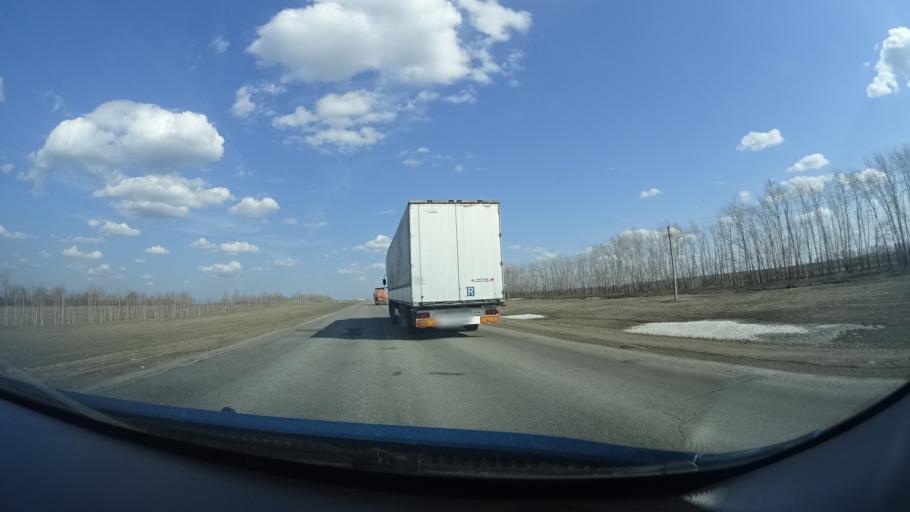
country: RU
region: Bashkortostan
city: Buzdyak
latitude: 54.6631
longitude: 54.7152
